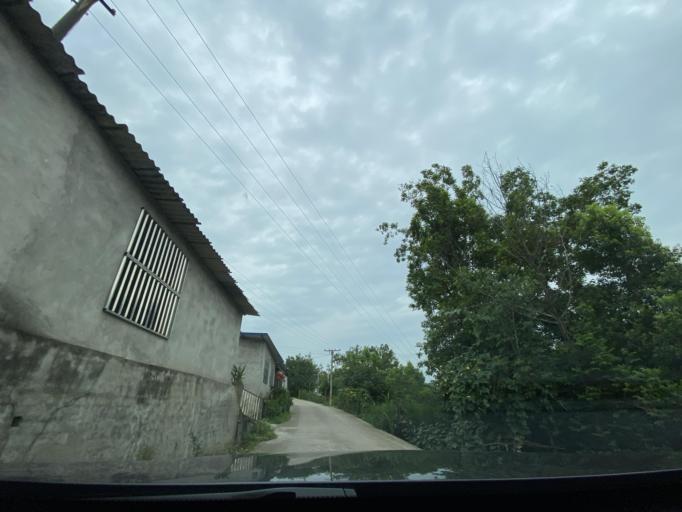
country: CN
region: Sichuan
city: Jiancheng
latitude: 30.3871
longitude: 104.4952
